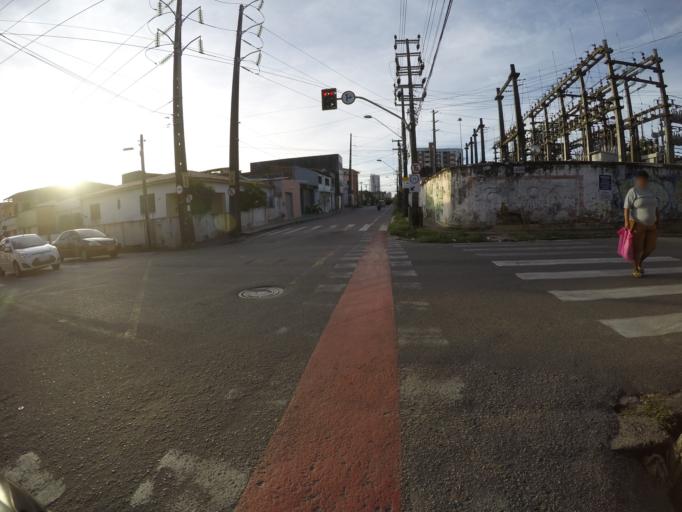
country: BR
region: Ceara
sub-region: Fortaleza
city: Fortaleza
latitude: -3.7540
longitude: -38.5147
